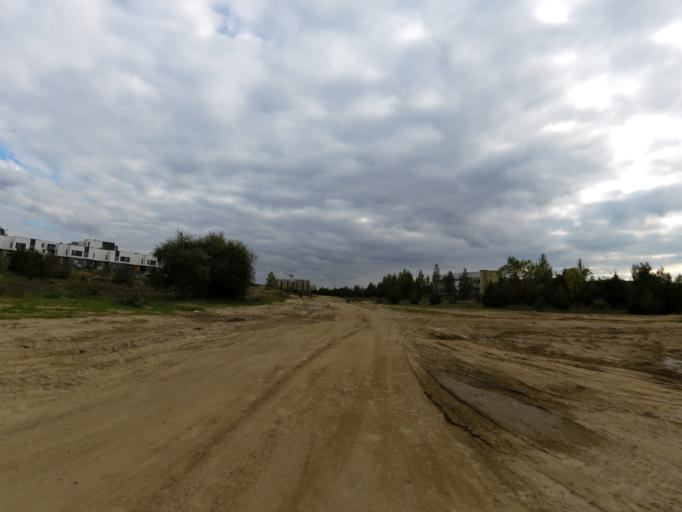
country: LT
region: Vilnius County
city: Pilaite
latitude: 54.7059
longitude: 25.1683
